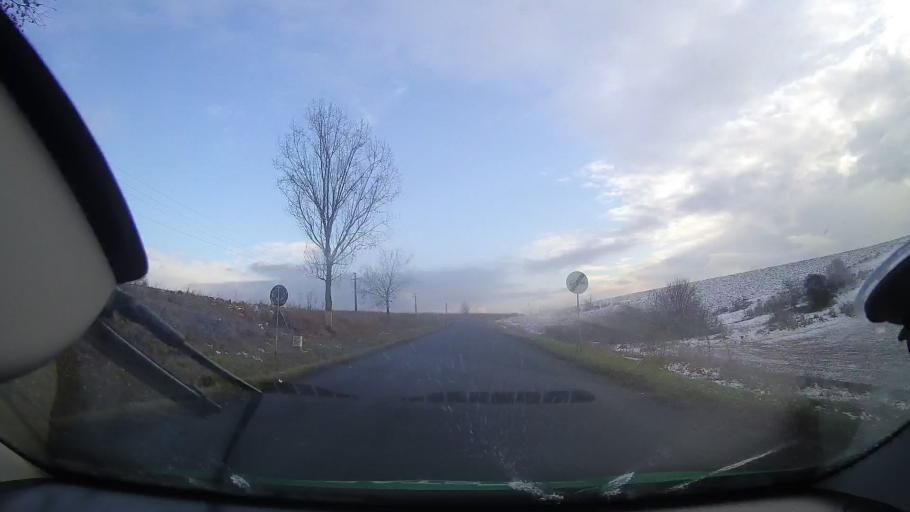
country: RO
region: Mures
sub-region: Comuna Cucerdea
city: Cucerdea
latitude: 46.4187
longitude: 24.2602
